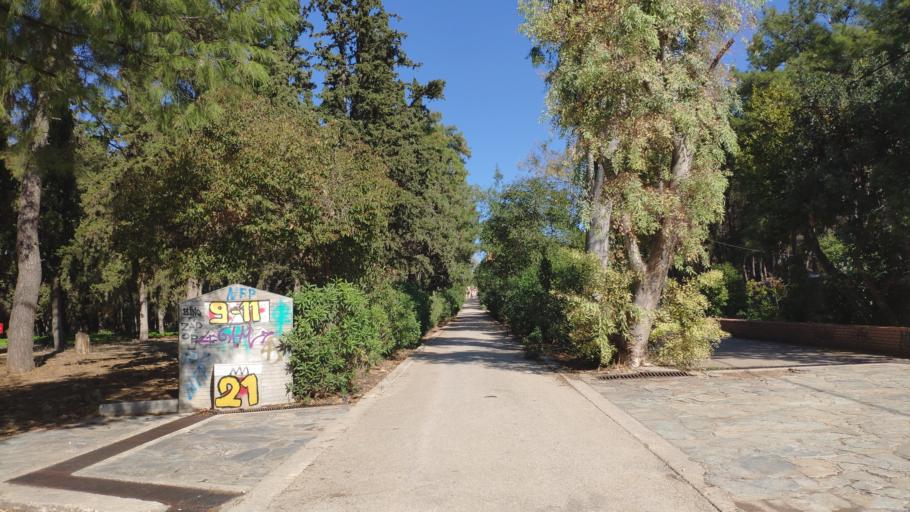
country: GR
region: Attica
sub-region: Nomarchia Athinas
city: Nea Filadelfeia
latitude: 38.0404
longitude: 23.7431
